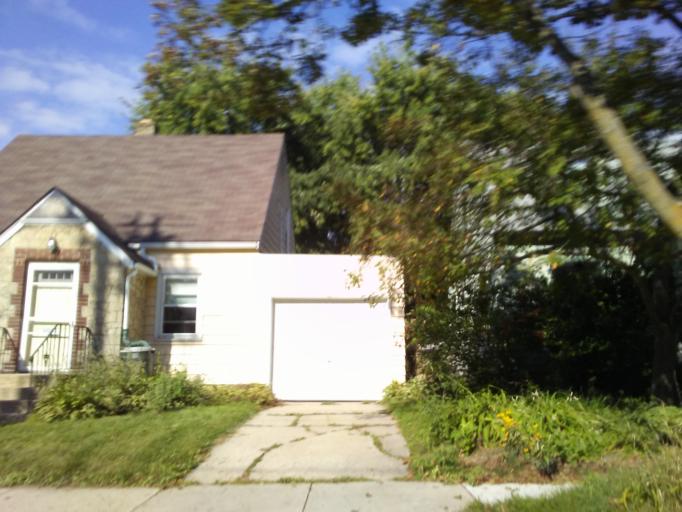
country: US
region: Wisconsin
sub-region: Dane County
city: Monona
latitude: 43.0994
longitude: -89.3440
